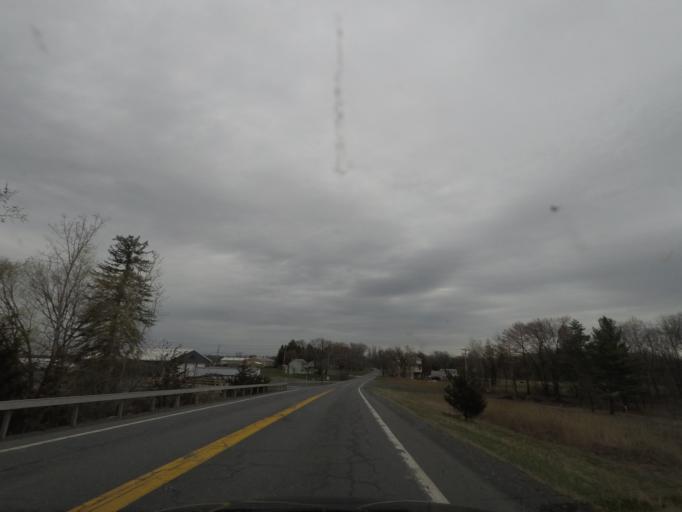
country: US
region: New York
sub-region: Rensselaer County
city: Castleton-on-Hudson
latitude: 42.5438
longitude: -73.8157
